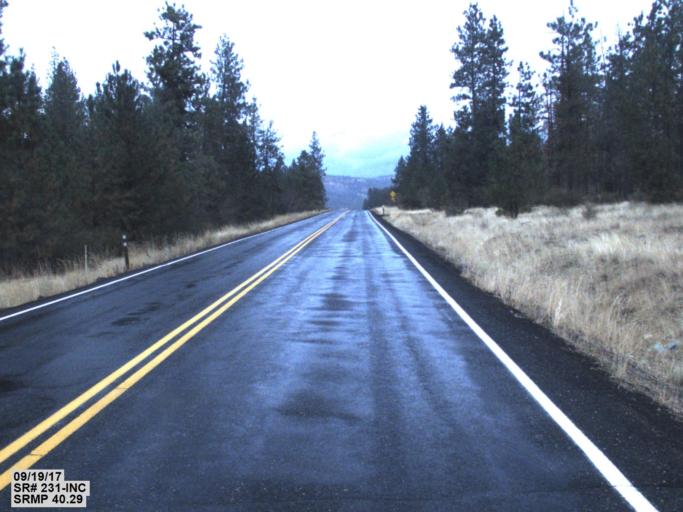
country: US
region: Washington
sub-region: Lincoln County
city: Davenport
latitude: 47.7934
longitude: -117.8907
